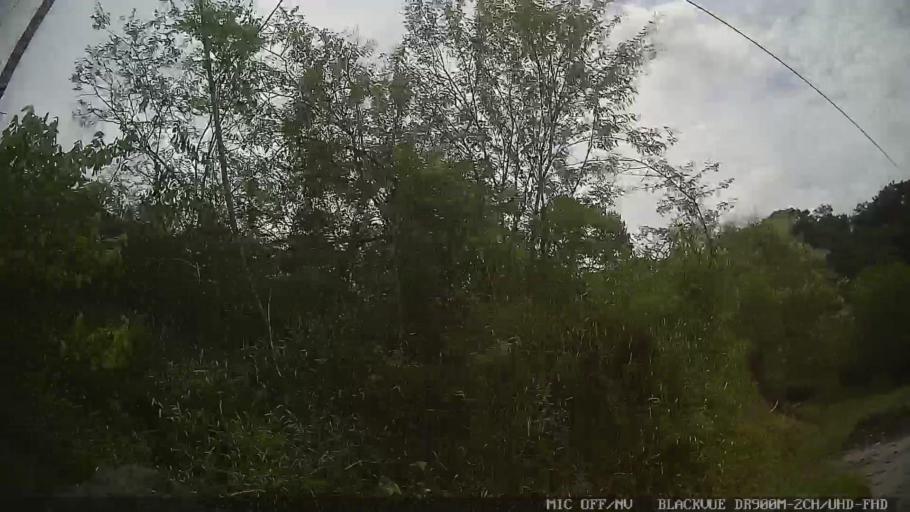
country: BR
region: Sao Paulo
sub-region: Santa Isabel
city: Santa Isabel
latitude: -23.3478
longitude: -46.2237
